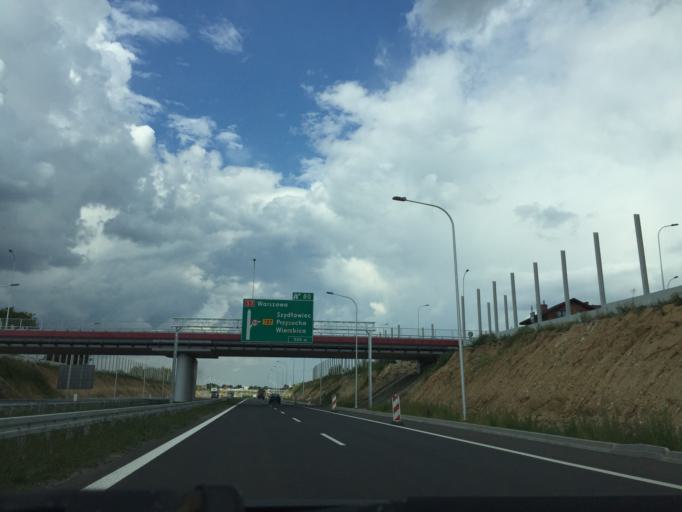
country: PL
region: Masovian Voivodeship
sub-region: Powiat szydlowiecki
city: Szydlowiec
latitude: 51.2290
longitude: 20.8731
